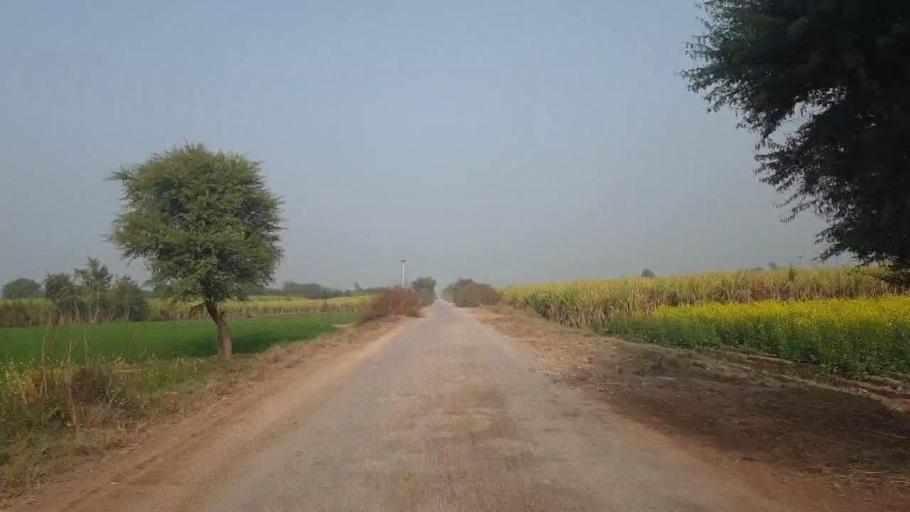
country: PK
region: Sindh
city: Shahdadpur
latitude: 25.8795
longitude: 68.5810
